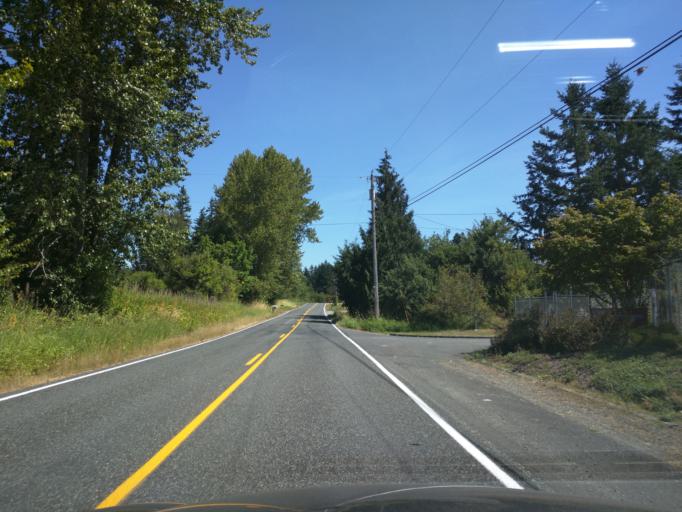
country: US
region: Washington
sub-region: Whatcom County
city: Geneva
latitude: 48.7982
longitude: -122.4236
